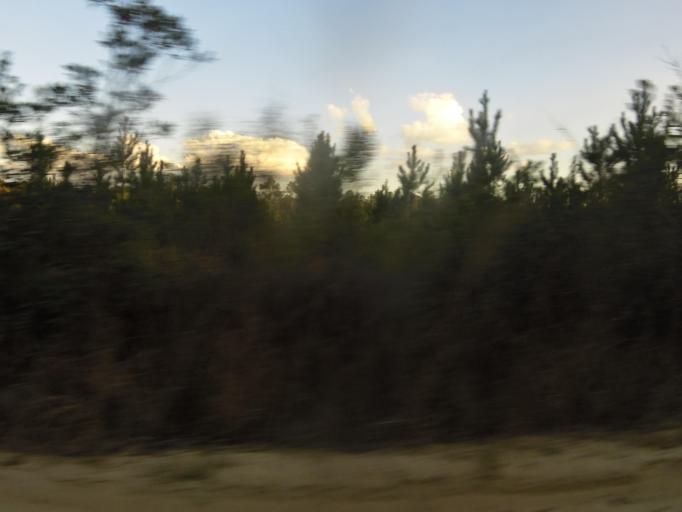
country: US
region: Florida
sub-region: Clay County
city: Keystone Heights
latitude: 29.8241
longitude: -81.8283
